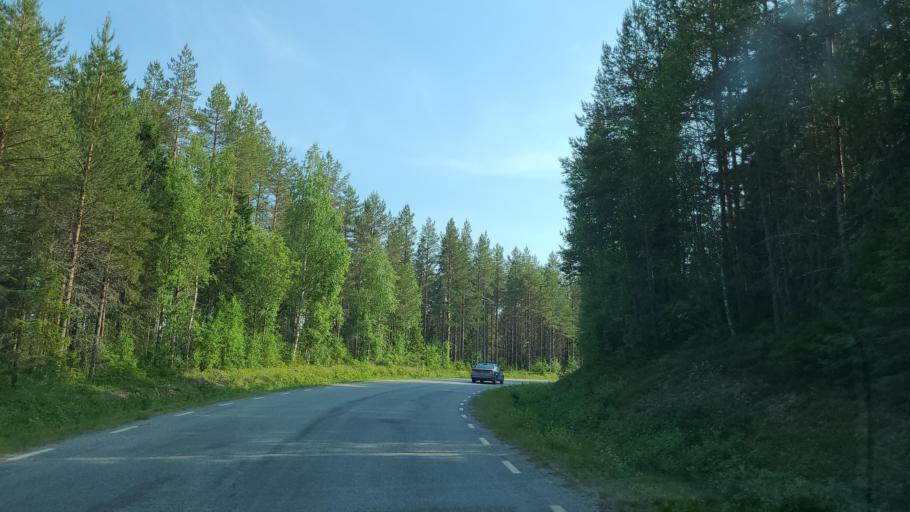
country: SE
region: Vaesterbotten
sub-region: Skelleftea Kommun
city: Burea
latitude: 64.3553
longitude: 21.3380
